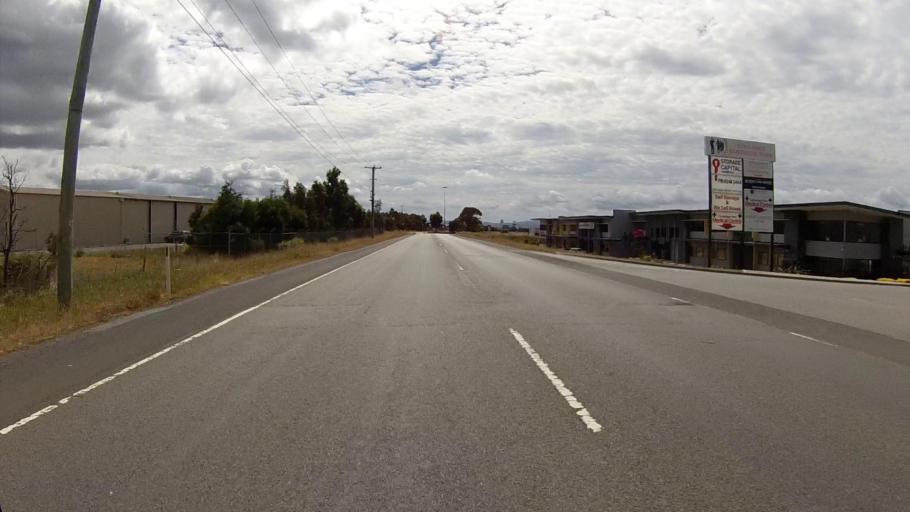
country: AU
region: Tasmania
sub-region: Clarence
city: Cambridge
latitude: -42.8319
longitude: 147.4625
